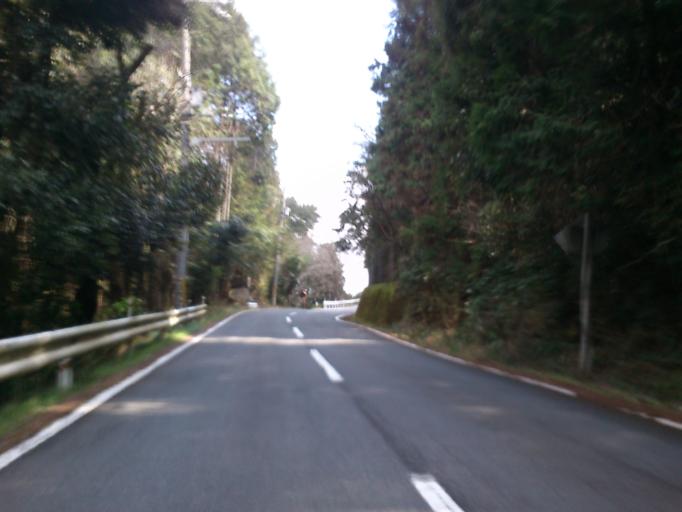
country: JP
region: Mie
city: Ueno-ebisumachi
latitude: 34.7350
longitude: 136.0013
